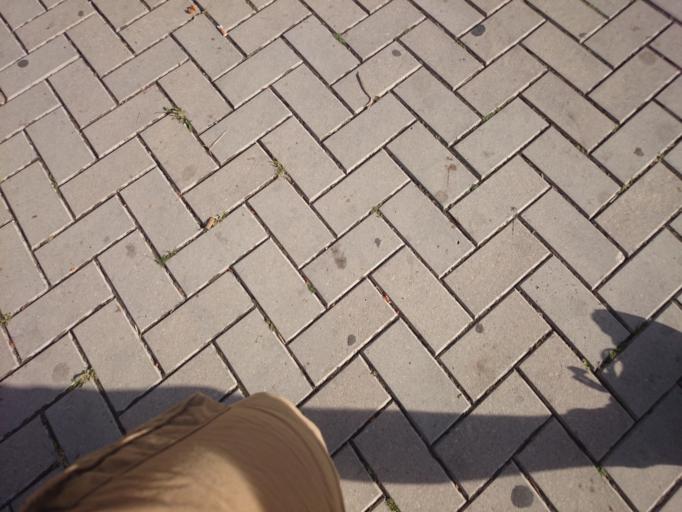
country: ME
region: Kotor
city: Kotor
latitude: 42.4345
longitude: 18.7666
